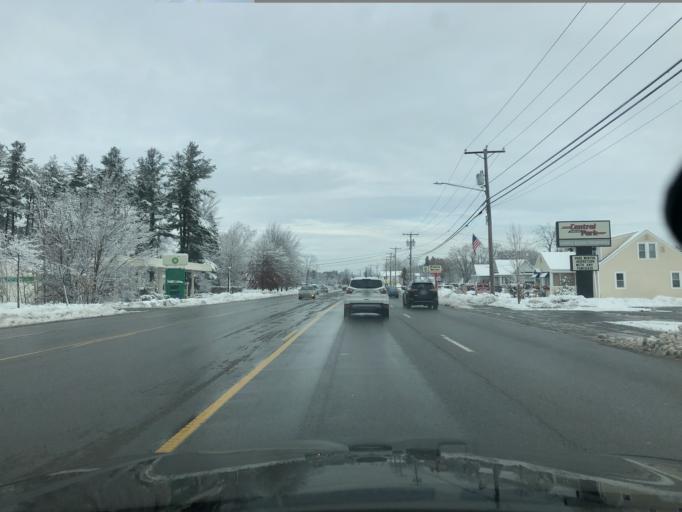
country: US
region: New Hampshire
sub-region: Strafford County
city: Dover
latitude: 43.2288
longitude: -70.8831
